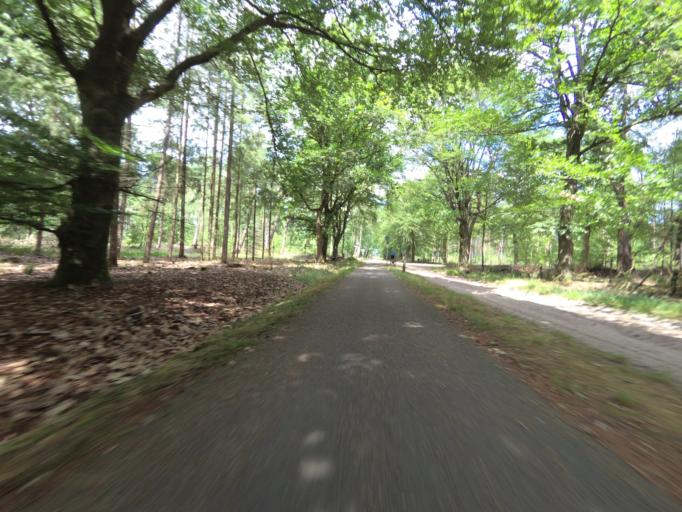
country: NL
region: Overijssel
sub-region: Gemeente Hof van Twente
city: Markelo
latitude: 52.3327
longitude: 6.4501
